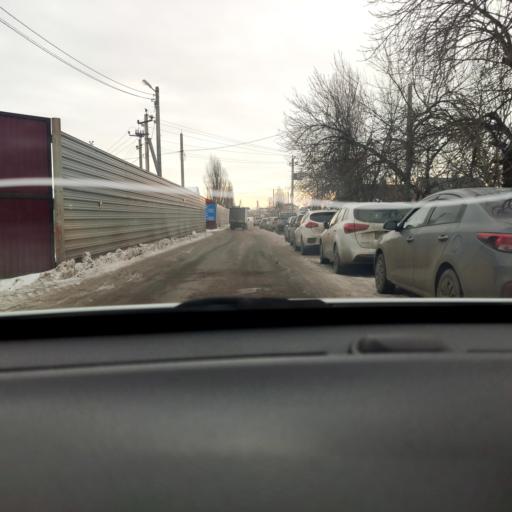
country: RU
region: Voronezj
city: Novaya Usman'
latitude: 51.6685
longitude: 39.3345
